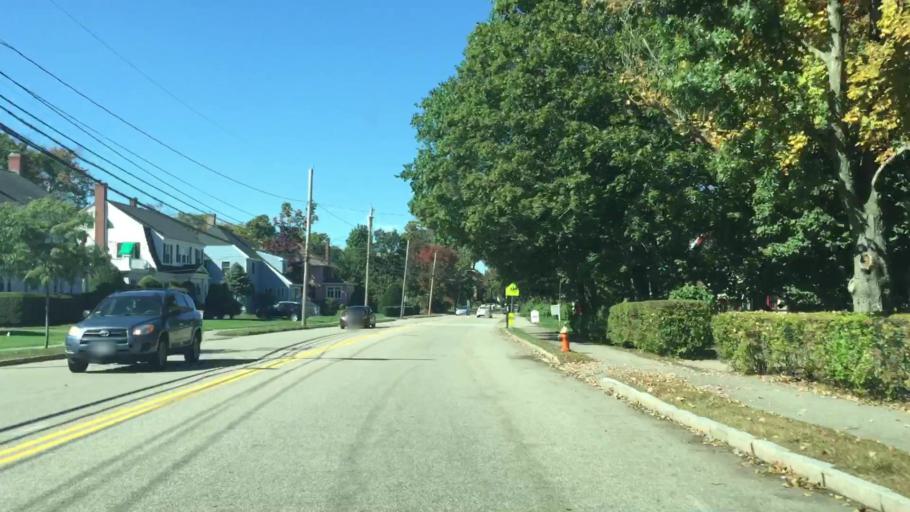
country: US
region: Massachusetts
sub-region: Essex County
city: North Andover
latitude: 42.6948
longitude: -71.1235
